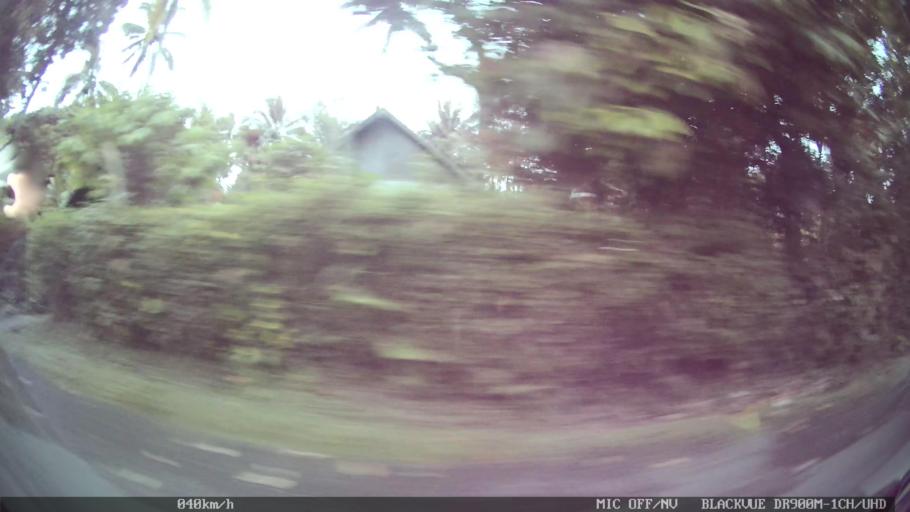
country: ID
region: Bali
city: Banjar Kubu
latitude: -8.4305
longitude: 115.4254
